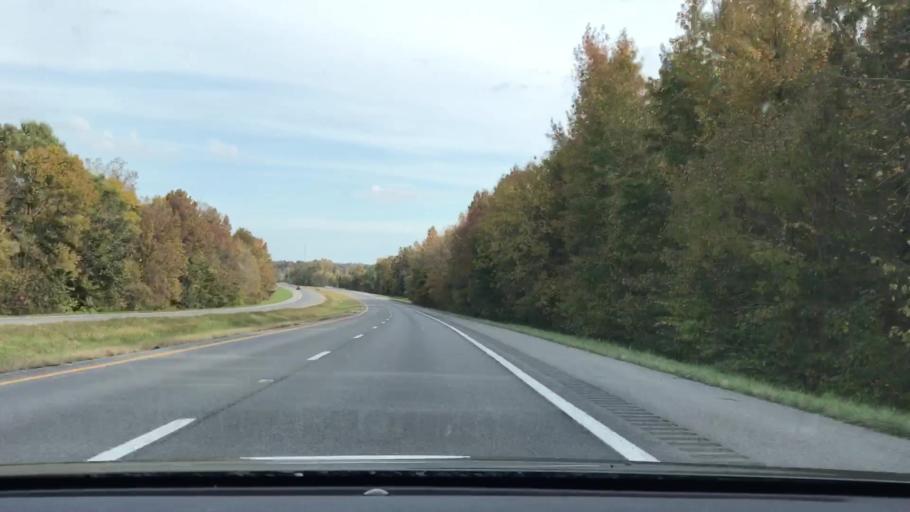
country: US
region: Kentucky
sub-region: Graves County
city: Mayfield
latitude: 36.8014
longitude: -88.4986
